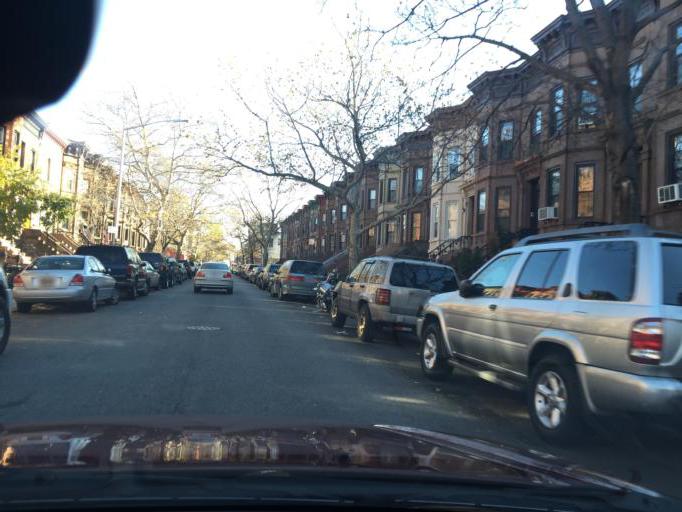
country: US
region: New York
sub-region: Kings County
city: Bensonhurst
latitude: 40.6428
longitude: -74.0155
